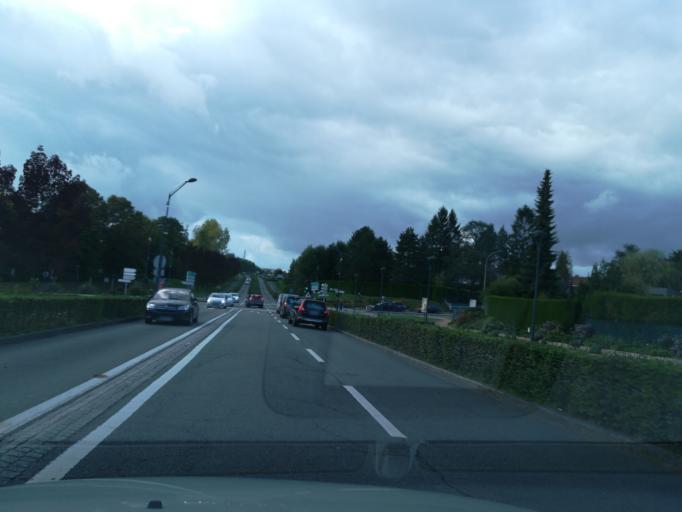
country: FR
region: Haute-Normandie
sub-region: Departement de la Seine-Maritime
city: Bois-Guillaume
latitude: 49.4722
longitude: 1.1130
